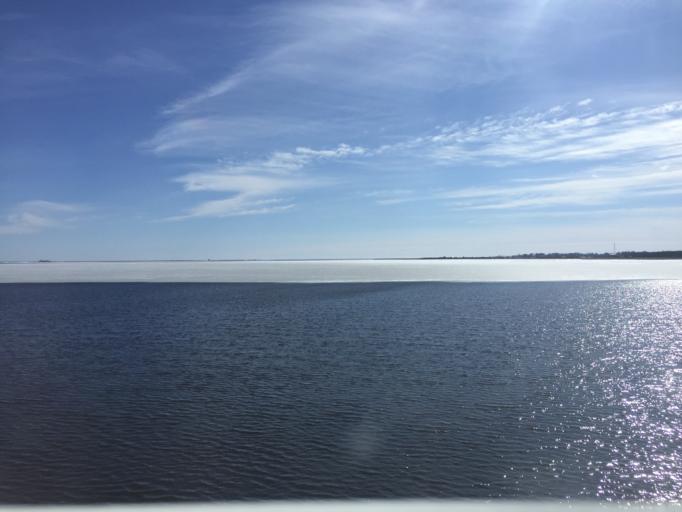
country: EE
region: Saare
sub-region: Orissaare vald
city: Orissaare
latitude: 58.5735
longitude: 23.3992
